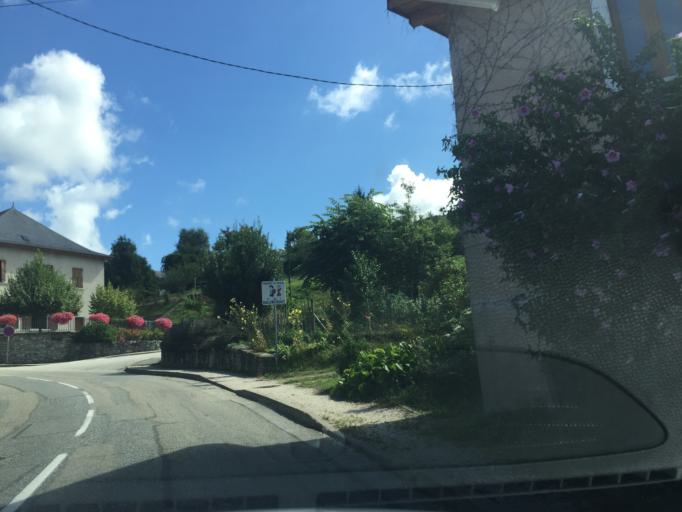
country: FR
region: Rhone-Alpes
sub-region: Departement de la Savoie
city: La Rochette
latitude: 45.4539
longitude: 6.1377
